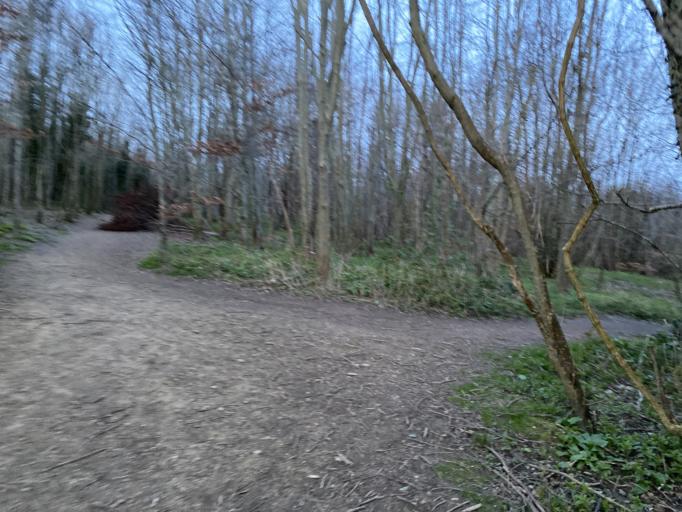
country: GB
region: England
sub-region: Brighton and Hove
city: Brighton
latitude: 50.8663
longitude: -0.0942
